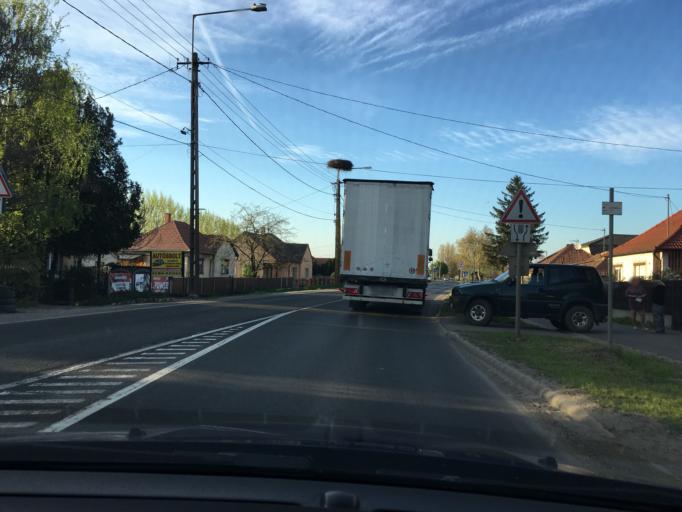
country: HU
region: Hajdu-Bihar
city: Mikepercs
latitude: 47.4483
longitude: 21.6325
